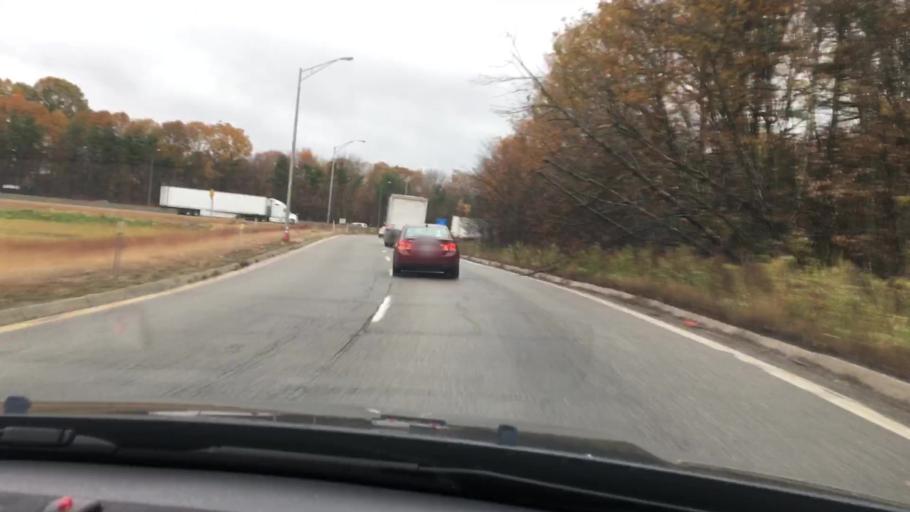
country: US
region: Massachusetts
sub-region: Worcester County
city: Westborough
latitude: 42.2646
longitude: -71.5727
